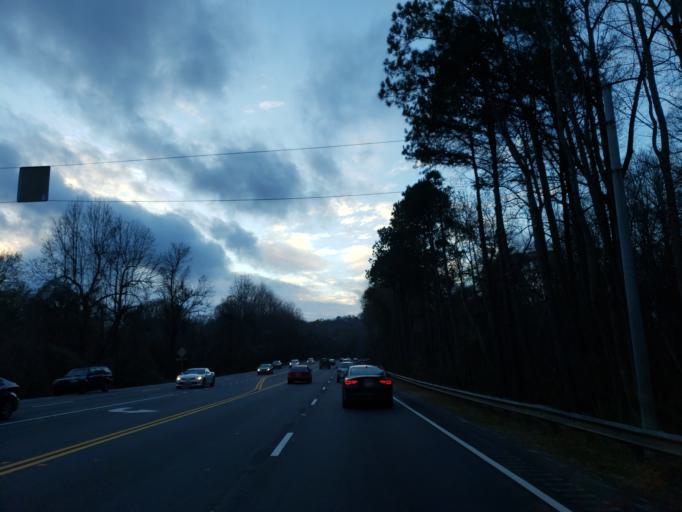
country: US
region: Georgia
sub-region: Fulton County
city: Union City
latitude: 33.6592
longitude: -84.5305
